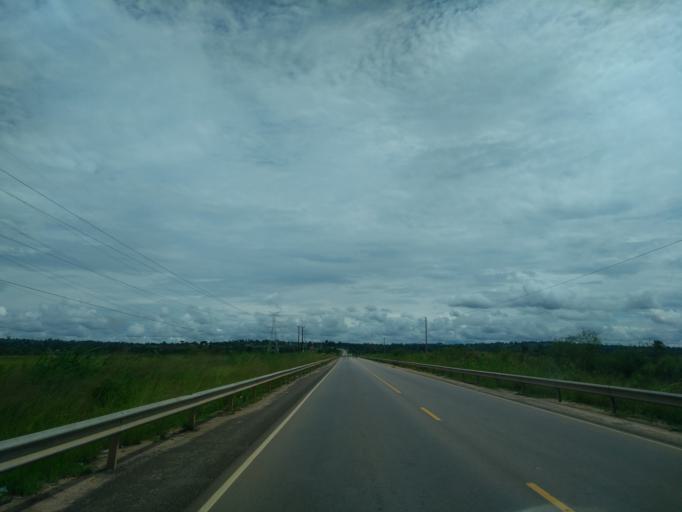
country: UG
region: Central Region
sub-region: Gomba District
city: Kanoni
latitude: -0.0323
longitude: 32.0100
